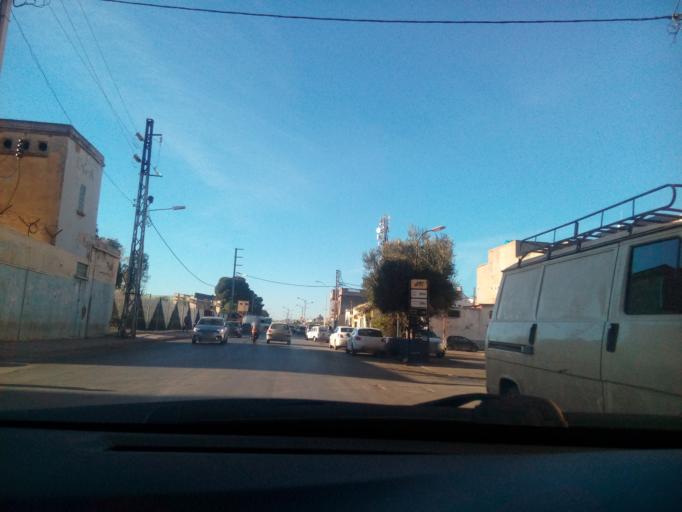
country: DZ
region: Oran
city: Oran
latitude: 35.6858
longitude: -0.6674
